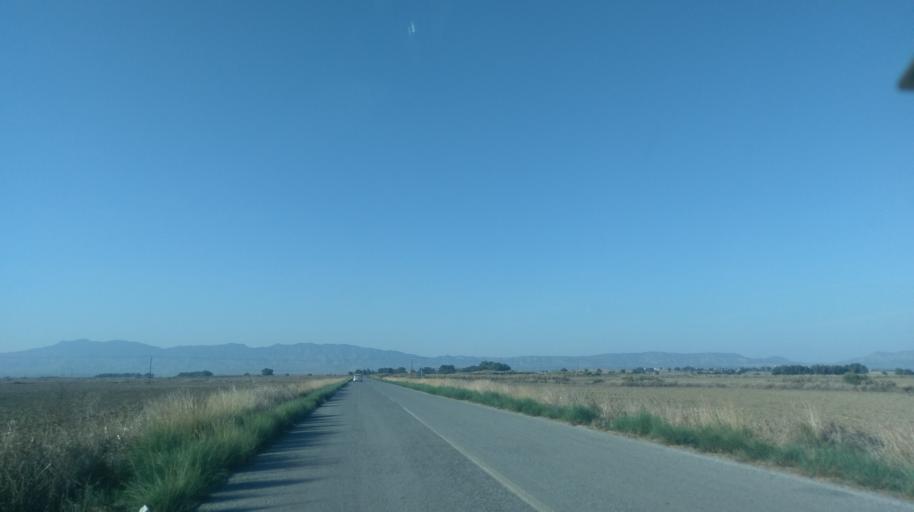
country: CY
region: Ammochostos
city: Lefkonoiko
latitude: 35.1914
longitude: 33.6988
